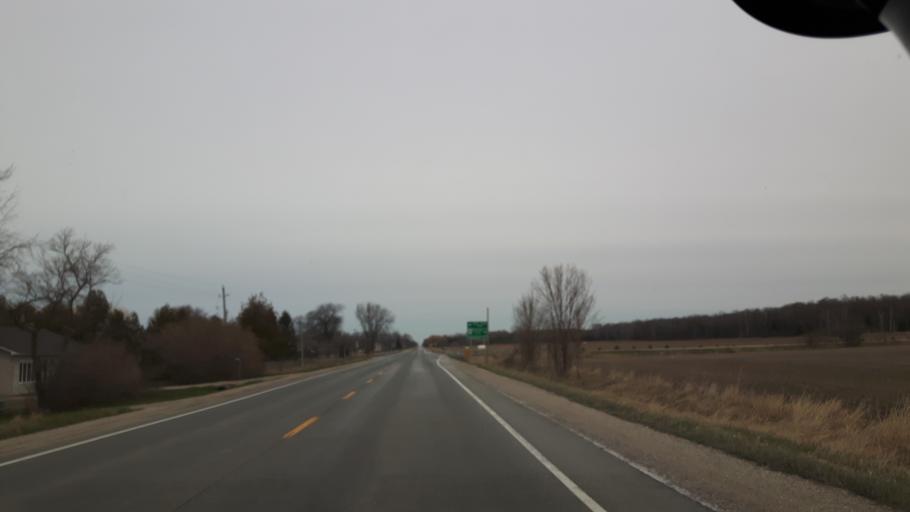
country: CA
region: Ontario
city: Goderich
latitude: 43.6410
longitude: -81.7056
